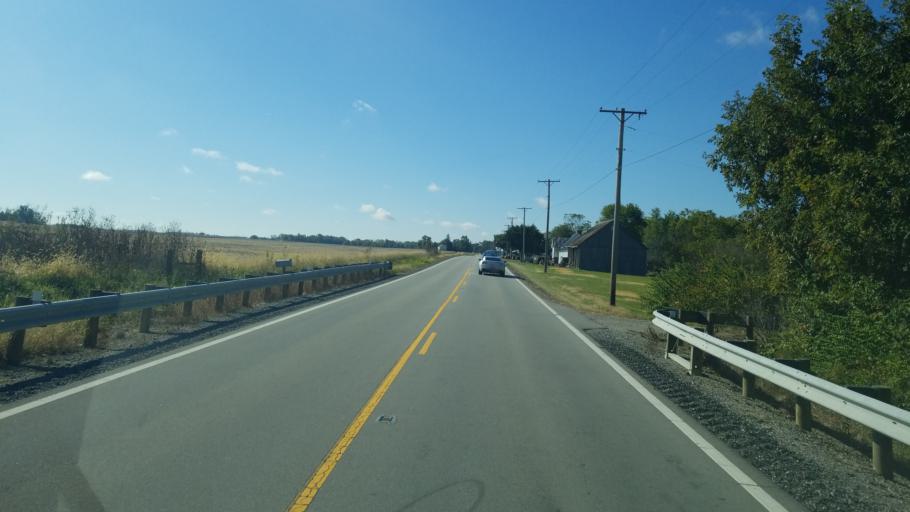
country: US
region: Ohio
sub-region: Fayette County
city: Washington Court House
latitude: 39.4706
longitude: -83.4853
